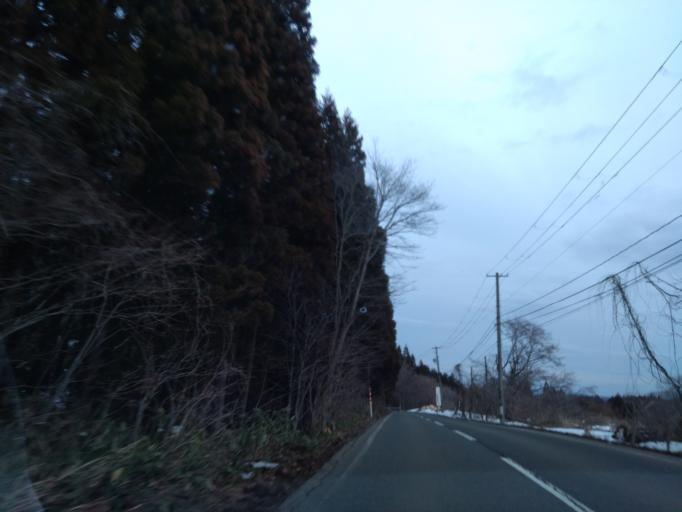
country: JP
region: Iwate
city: Kitakami
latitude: 39.2387
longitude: 140.9736
